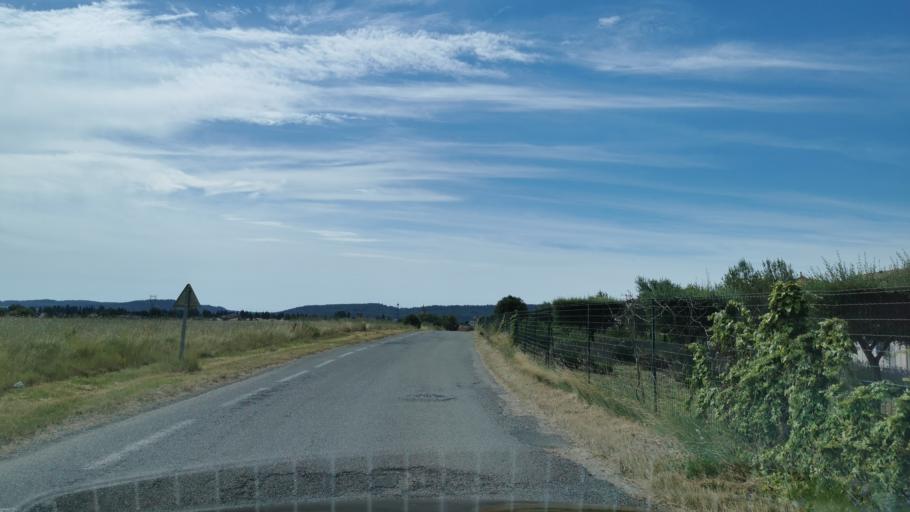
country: FR
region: Languedoc-Roussillon
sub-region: Departement de l'Herault
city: Olonzac
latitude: 43.2749
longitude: 2.7103
